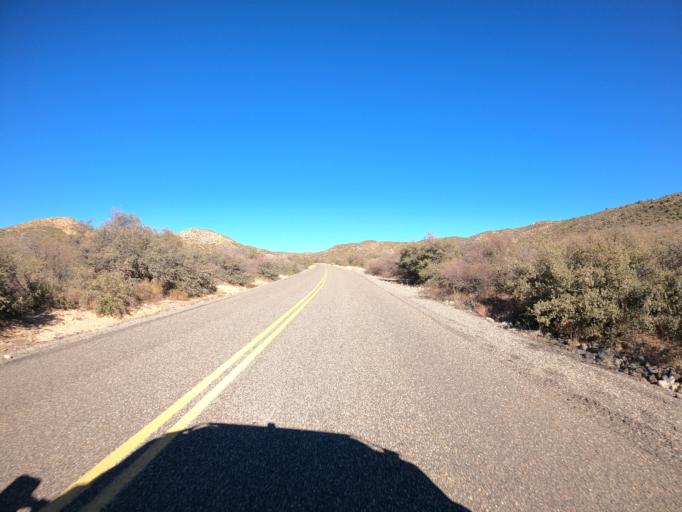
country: US
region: Arizona
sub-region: Yavapai County
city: Verde Village
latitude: 34.5593
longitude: -112.0744
